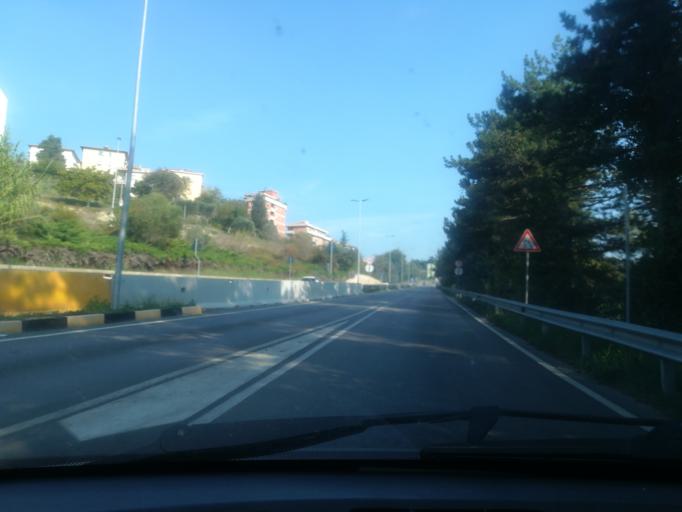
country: IT
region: The Marches
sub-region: Provincia di Macerata
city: Macerata
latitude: 43.2919
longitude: 13.4501
